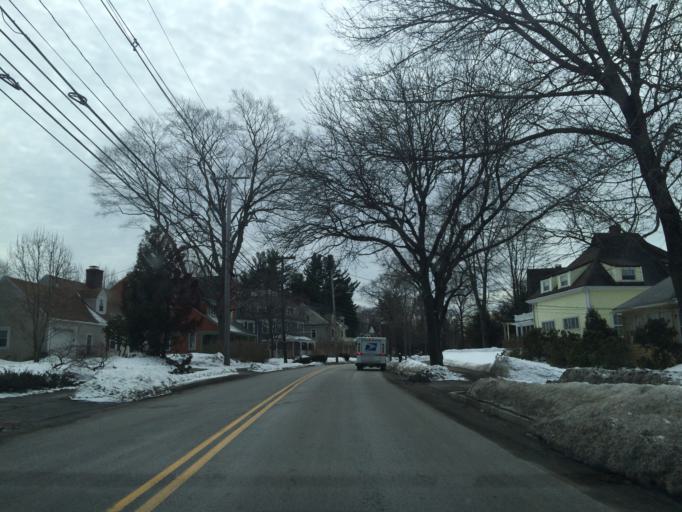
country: US
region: Massachusetts
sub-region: Middlesex County
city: Lexington
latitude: 42.4447
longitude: -71.2289
